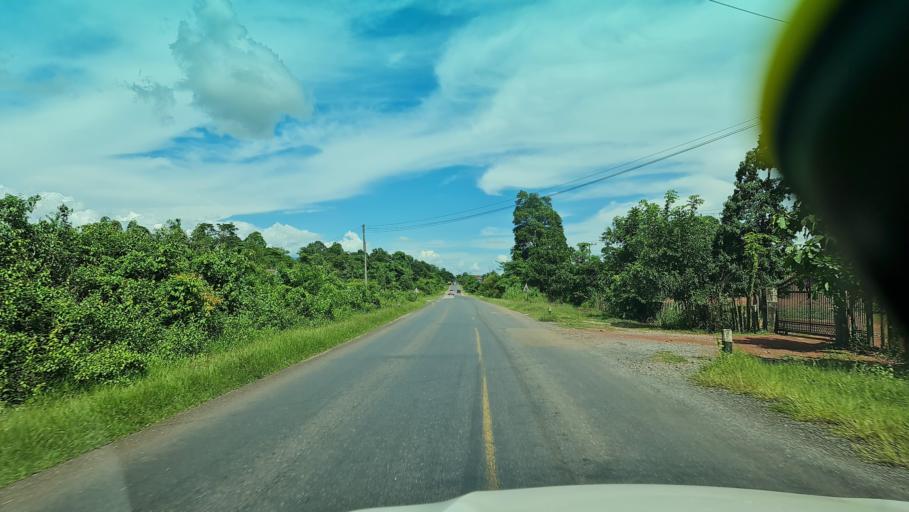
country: LA
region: Bolikhamxai
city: Pakkading
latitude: 18.2822
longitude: 104.0585
